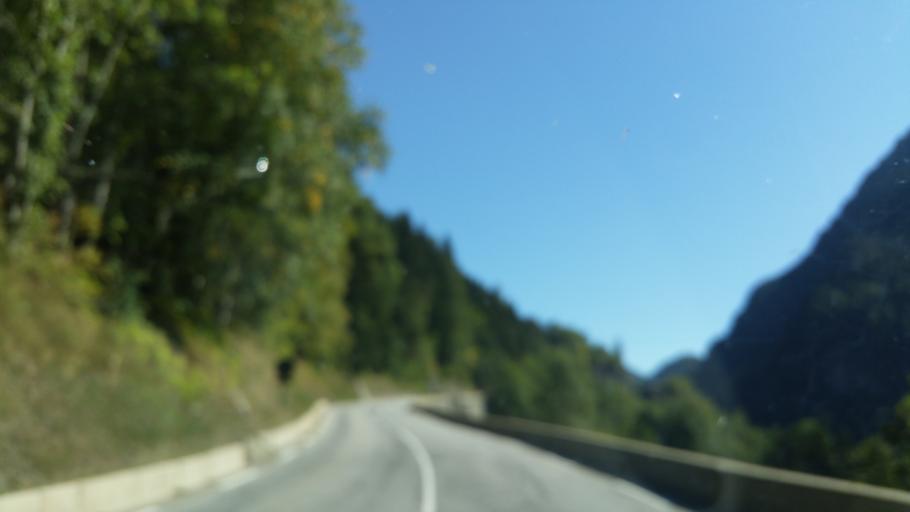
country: FR
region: Rhone-Alpes
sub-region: Departement de la Savoie
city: Tignes
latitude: 45.5705
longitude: 6.8871
